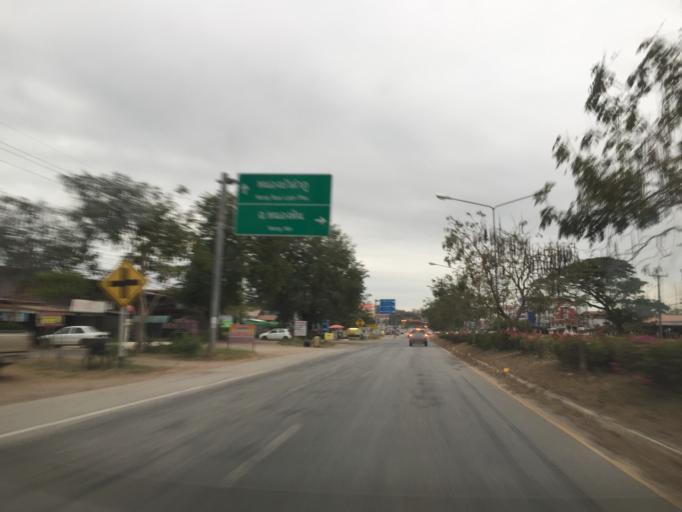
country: TH
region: Loei
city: Erawan
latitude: 17.3027
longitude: 101.9539
